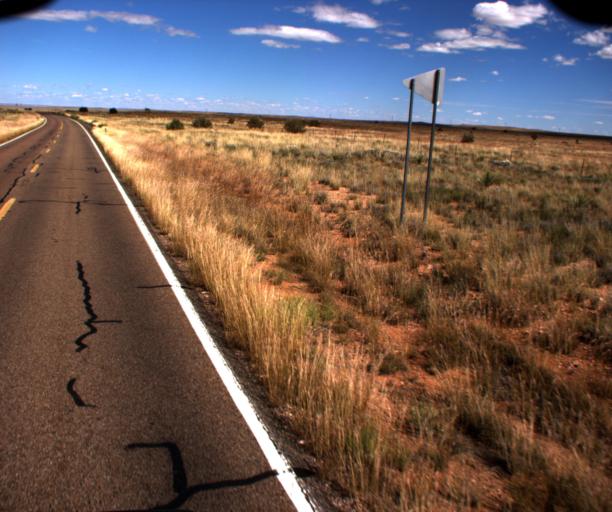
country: US
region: Arizona
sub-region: Navajo County
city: Holbrook
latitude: 34.7540
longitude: -110.2545
